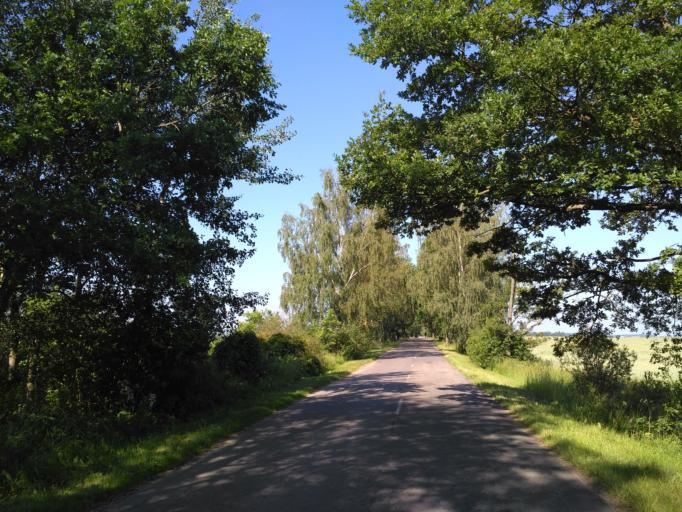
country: BY
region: Minsk
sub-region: Smalyavitski Rayon
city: Oktjabr'skij
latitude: 53.9586
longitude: 28.2713
